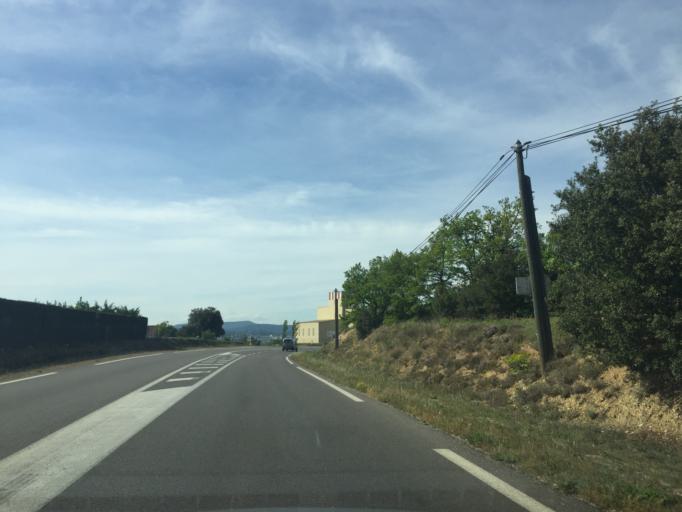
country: FR
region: Provence-Alpes-Cote d'Azur
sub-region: Departement du Var
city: Vinon-sur-Verdon
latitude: 43.7400
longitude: 5.8004
